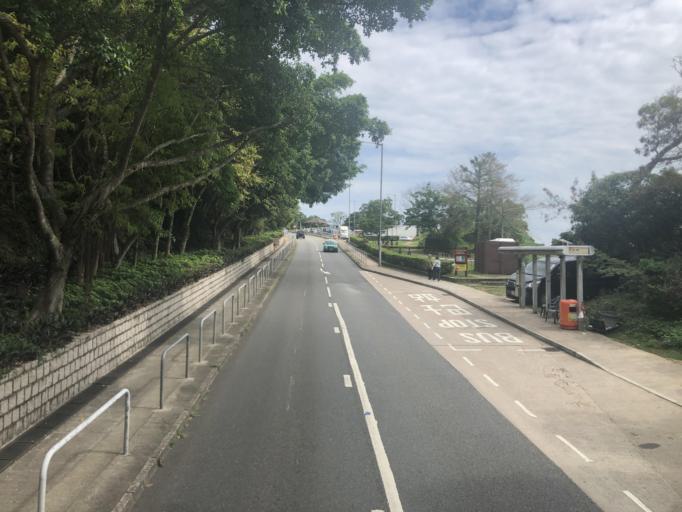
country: HK
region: Sai Kung
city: Sai Kung
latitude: 22.3927
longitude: 114.2894
